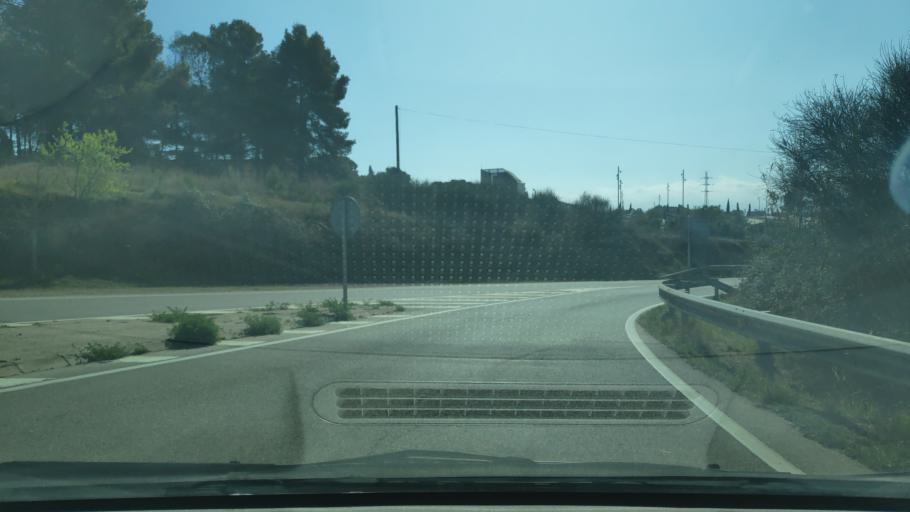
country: ES
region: Catalonia
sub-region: Provincia de Barcelona
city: Sabadell
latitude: 41.5600
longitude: 2.1213
